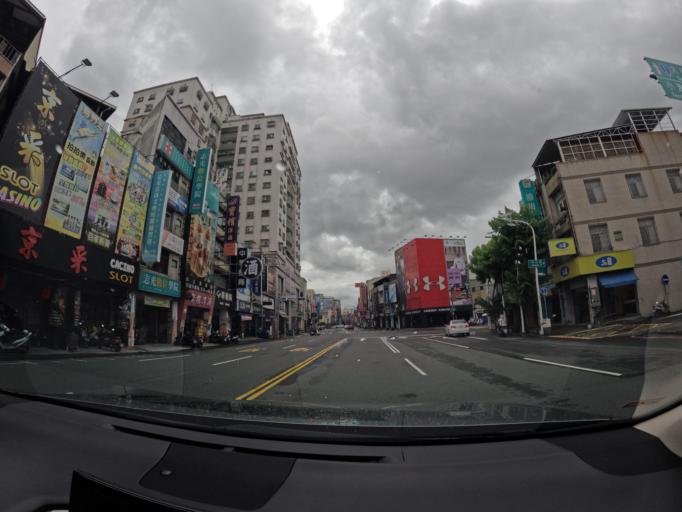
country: TW
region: Taiwan
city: Fengshan
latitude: 22.6259
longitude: 120.3561
